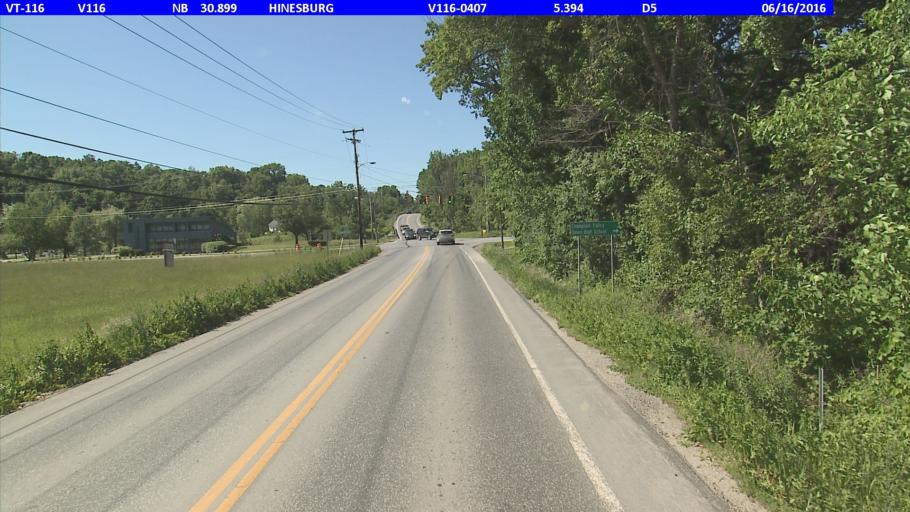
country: US
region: Vermont
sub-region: Chittenden County
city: Hinesburg
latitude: 44.3404
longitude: -73.1159
